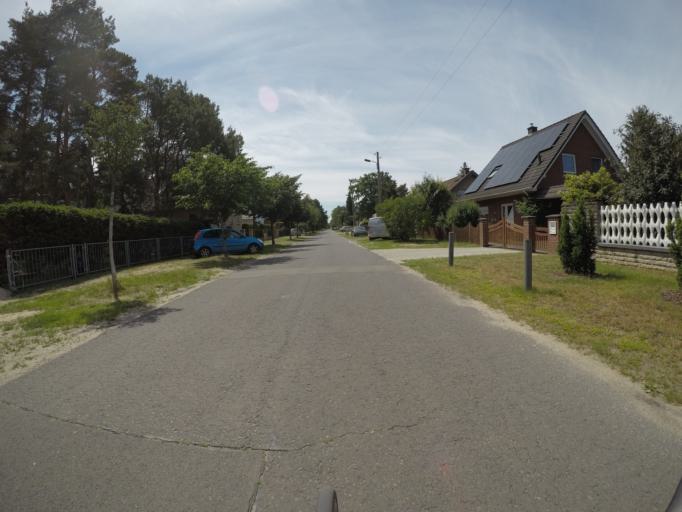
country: DE
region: Berlin
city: Mahlsdorf
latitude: 52.4807
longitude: 13.6121
